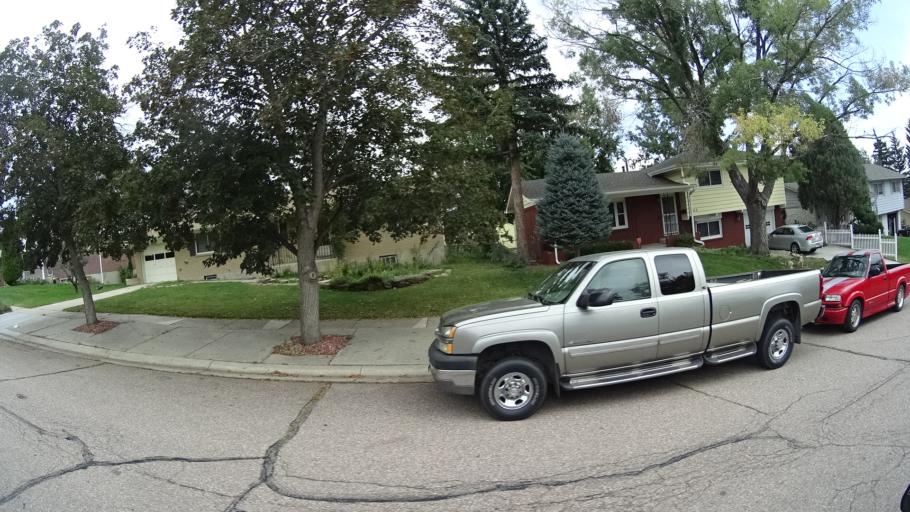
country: US
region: Colorado
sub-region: El Paso County
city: Colorado Springs
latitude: 38.8604
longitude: -104.7852
